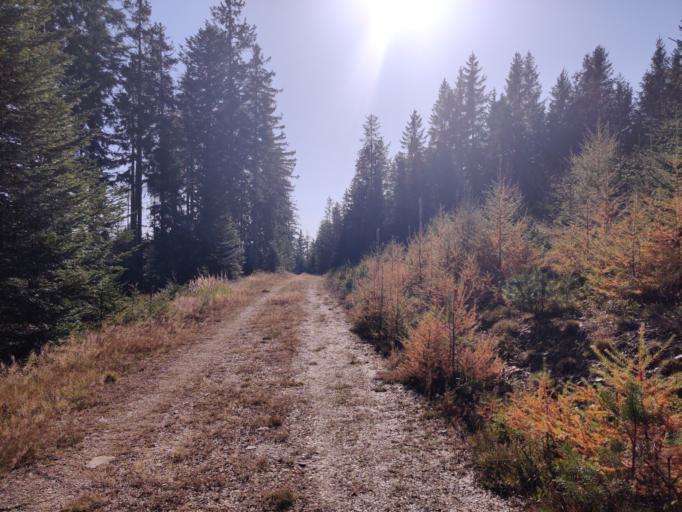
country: AT
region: Styria
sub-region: Politischer Bezirk Hartberg-Fuerstenfeld
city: Sankt Jakob im Walde
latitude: 47.4729
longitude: 15.8079
